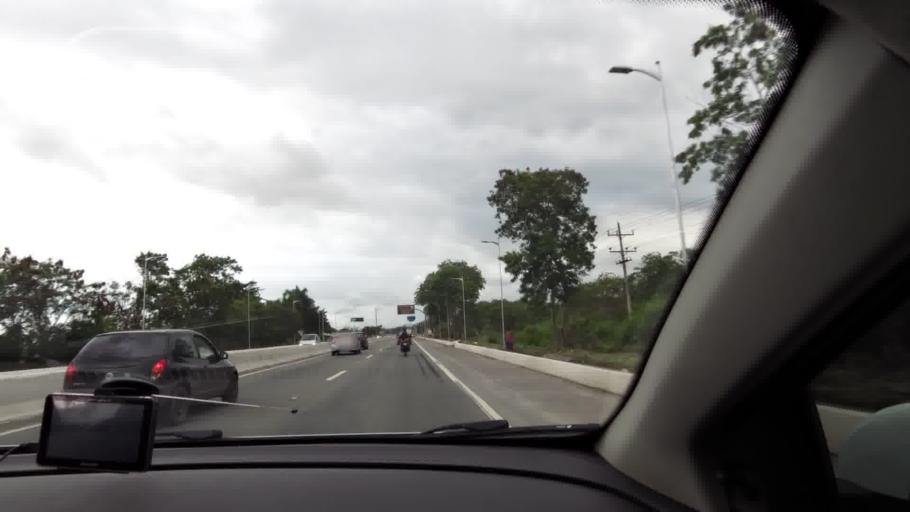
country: BR
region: Espirito Santo
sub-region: Vila Velha
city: Vila Velha
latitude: -20.2525
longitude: -40.2877
